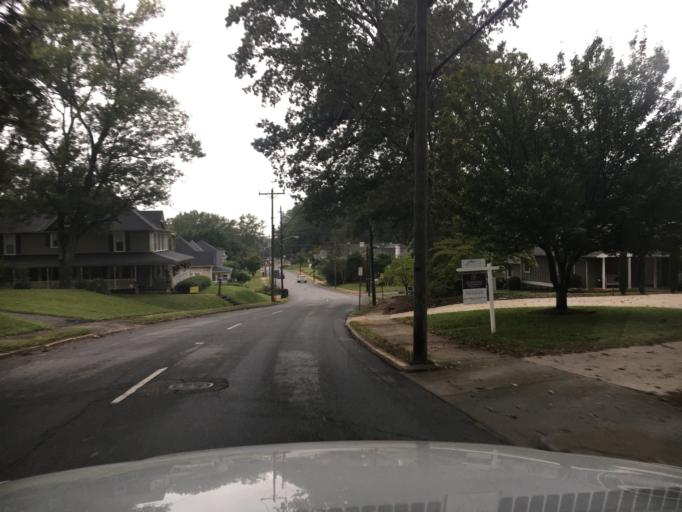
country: US
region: North Carolina
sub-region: Catawba County
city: Hickory
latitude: 35.7357
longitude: -81.3479
